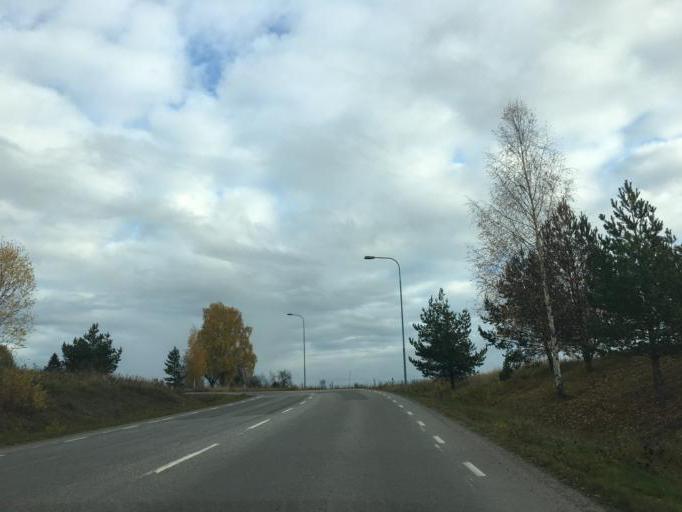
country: SE
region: Vaestmanland
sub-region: Vasteras
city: Skultuna
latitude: 59.5747
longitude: 16.3985
